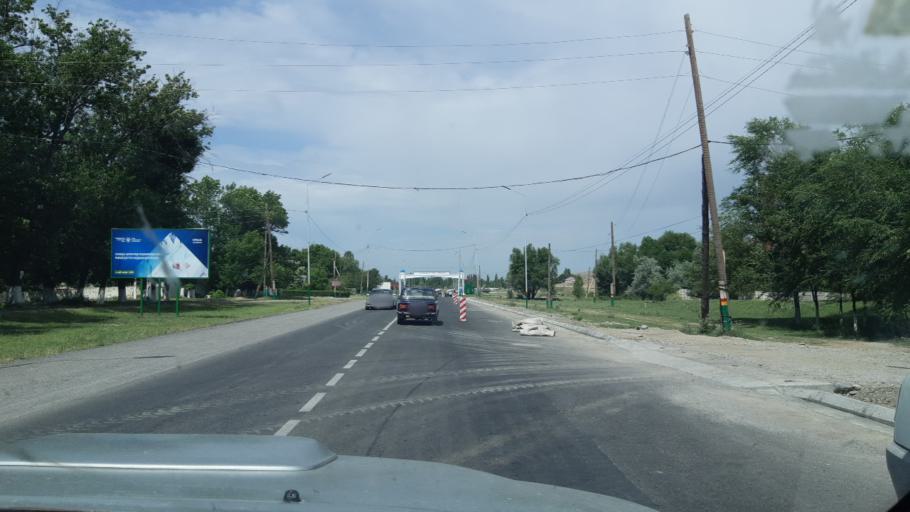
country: KZ
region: Ongtustik Qazaqstan
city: Turar Ryskulov
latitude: 42.5490
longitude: 70.3078
